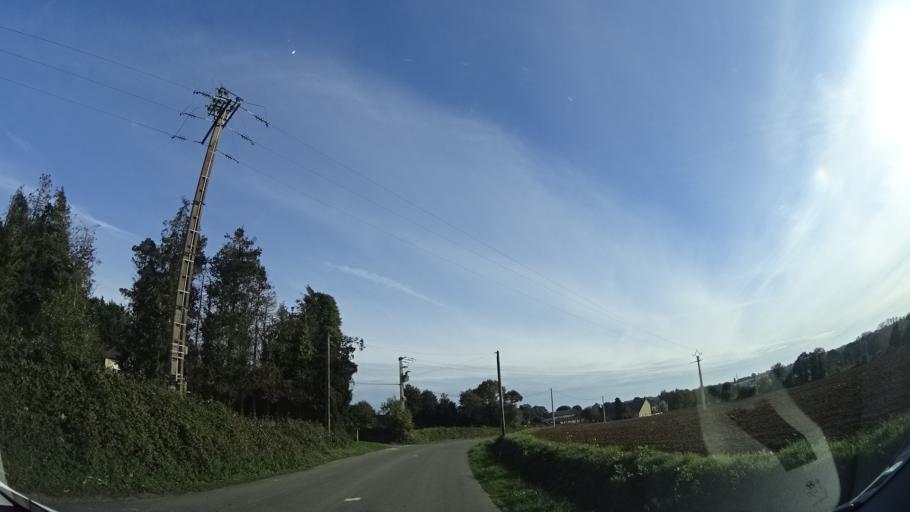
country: FR
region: Brittany
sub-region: Departement d'Ille-et-Vilaine
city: Geveze
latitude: 48.2253
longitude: -1.8146
